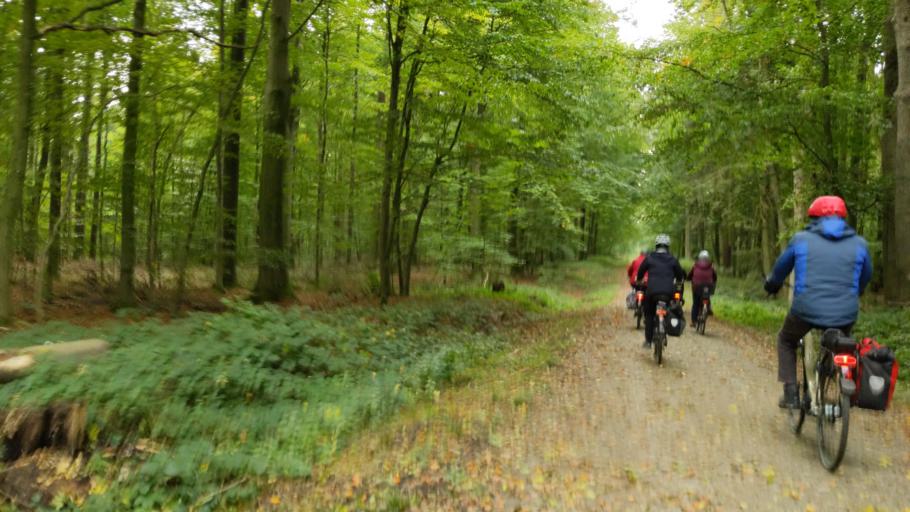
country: DE
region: Schleswig-Holstein
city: Rehhorst
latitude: 53.8551
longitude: 10.4681
